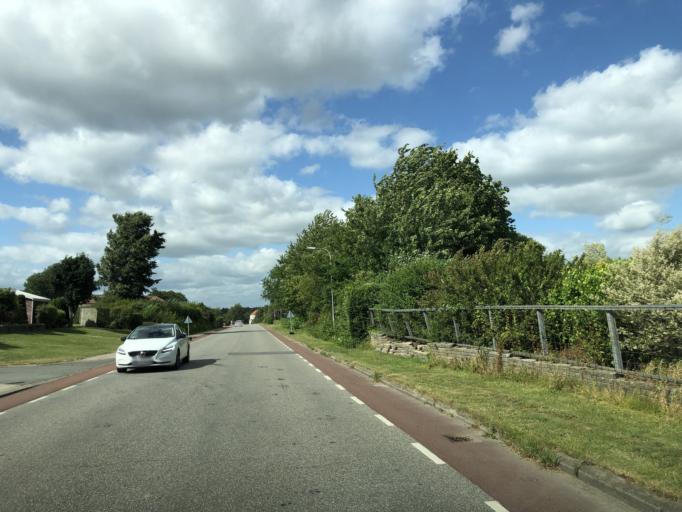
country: DK
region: South Denmark
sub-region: Vejle Kommune
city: Borkop
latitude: 55.6382
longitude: 9.6529
